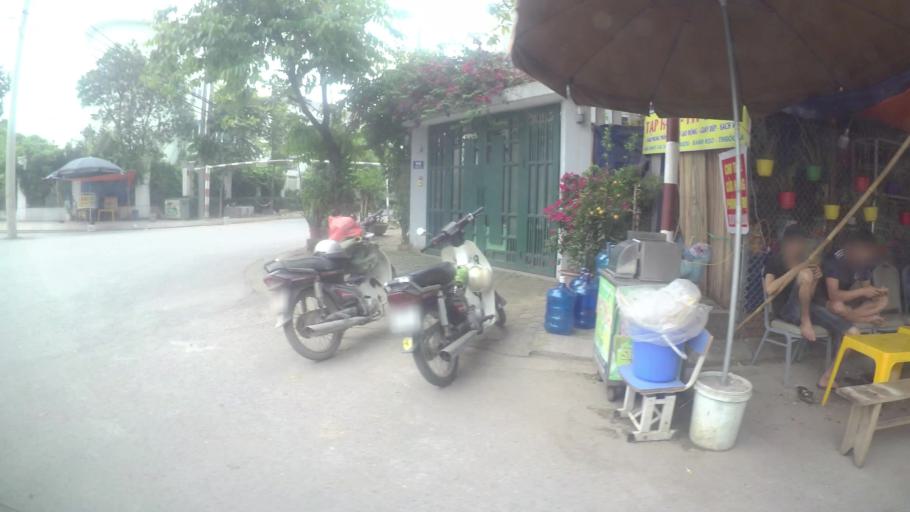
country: VN
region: Ha Noi
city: Ha Dong
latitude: 20.9817
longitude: 105.7674
